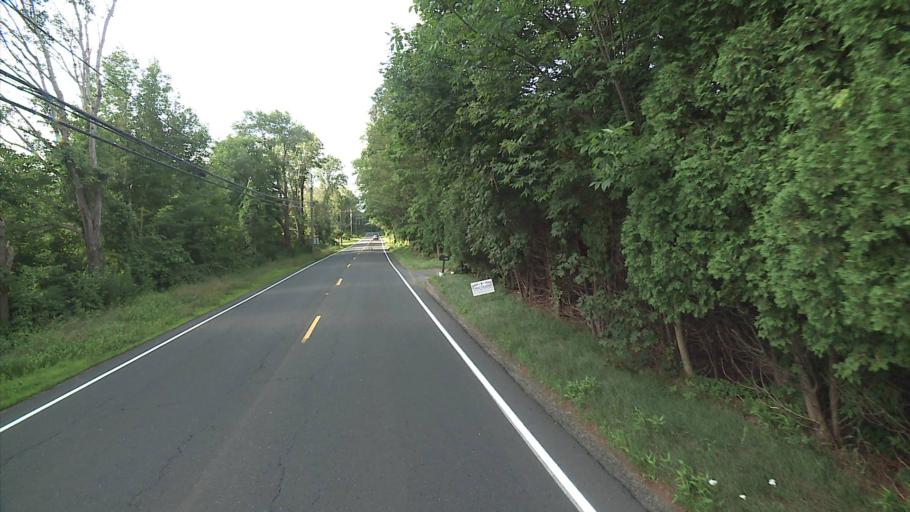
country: US
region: Connecticut
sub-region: Middlesex County
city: Higganum
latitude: 41.3950
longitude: -72.5624
